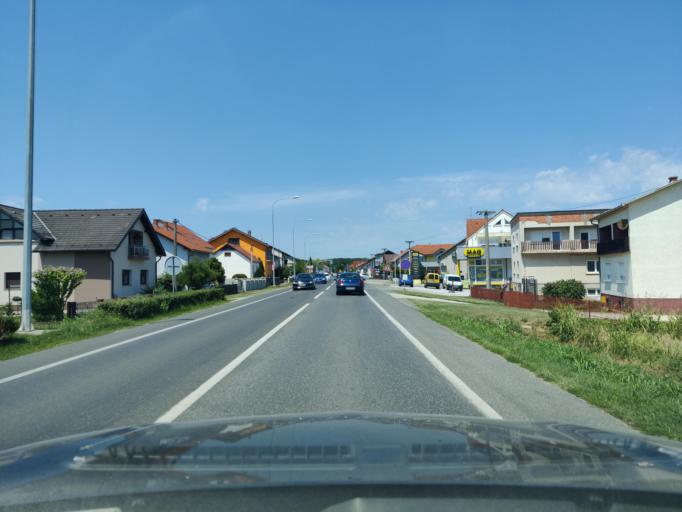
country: HR
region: Medimurska
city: Senkovec
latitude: 46.4001
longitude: 16.4253
